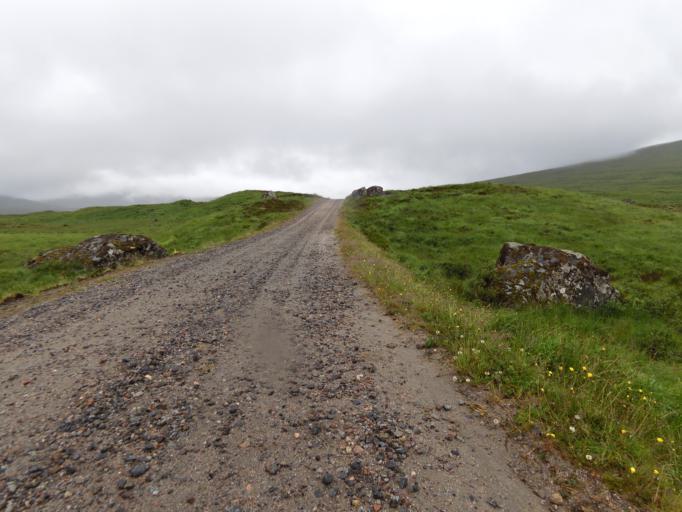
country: GB
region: Scotland
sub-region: Highland
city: Spean Bridge
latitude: 56.7657
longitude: -4.6726
